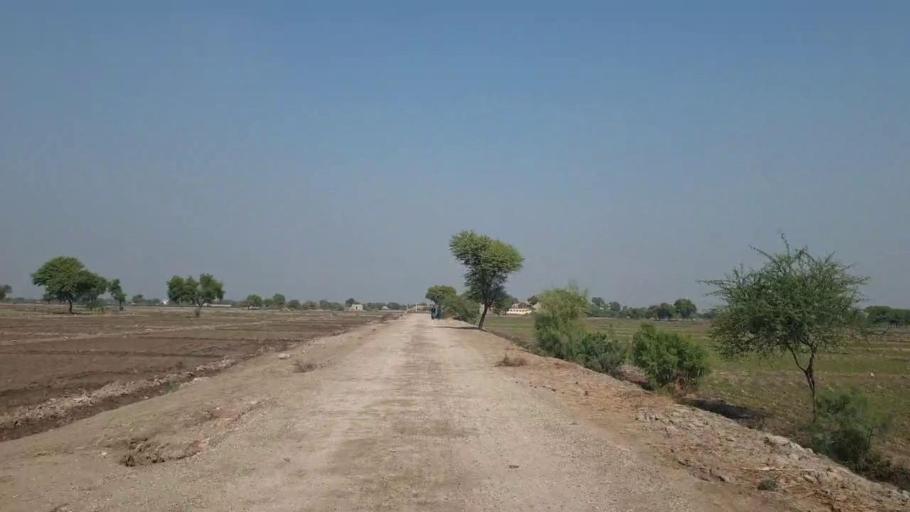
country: PK
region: Sindh
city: Sehwan
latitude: 26.4262
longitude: 67.7815
